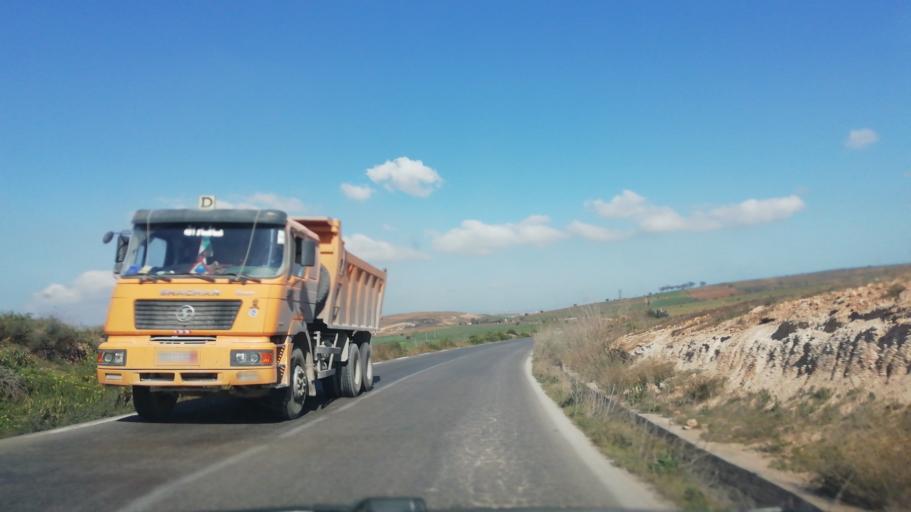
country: DZ
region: Oran
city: Ain el Bya
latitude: 35.7305
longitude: -0.2524
